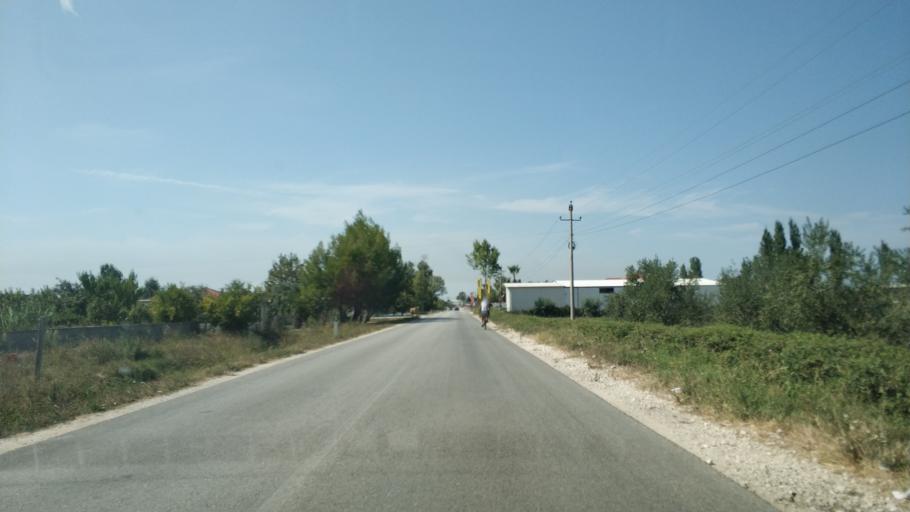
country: AL
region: Fier
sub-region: Rrethi i Fierit
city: Dermenas
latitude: 40.7401
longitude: 19.5100
